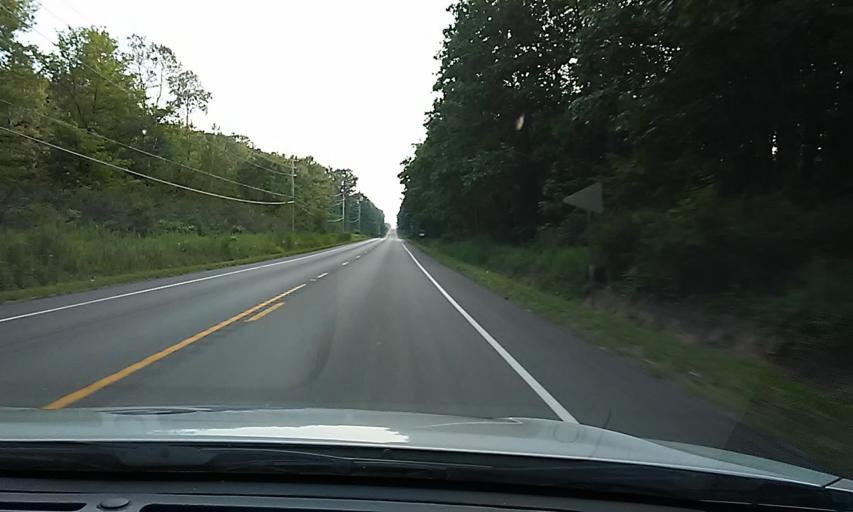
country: US
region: Pennsylvania
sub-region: Forest County
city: Marienville
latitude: 41.4922
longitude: -79.0929
